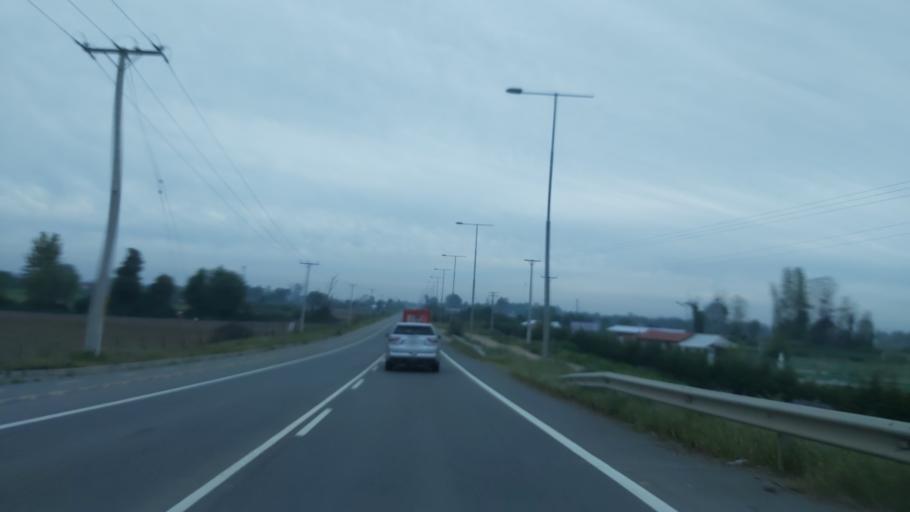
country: CL
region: Maule
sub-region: Provincia de Linares
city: Linares
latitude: -35.8271
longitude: -71.6040
